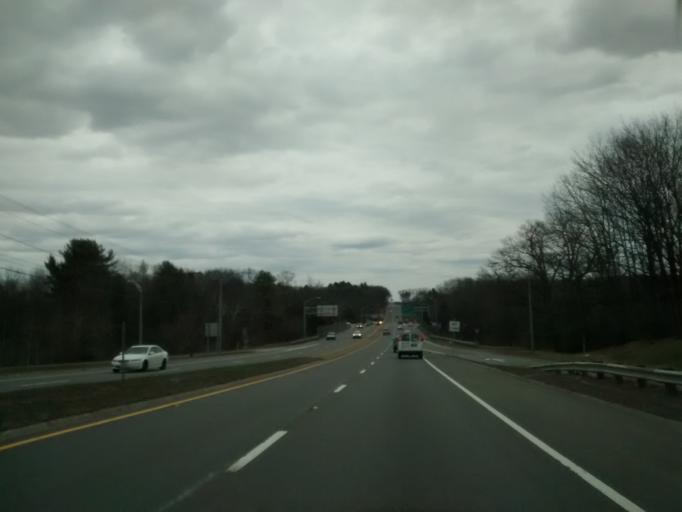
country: US
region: Massachusetts
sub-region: Worcester County
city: Auburn
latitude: 42.1837
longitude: -71.8492
